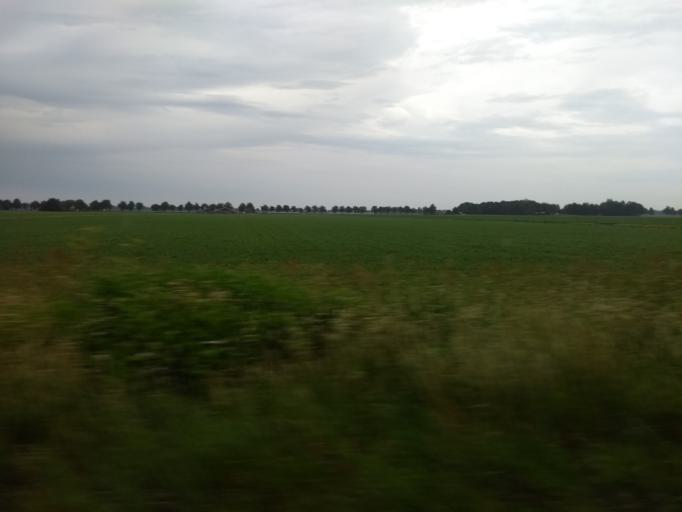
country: NL
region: Overijssel
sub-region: Gemeente Twenterand
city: Westerhaar-Vriezenveensewijk
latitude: 52.4889
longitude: 6.5991
